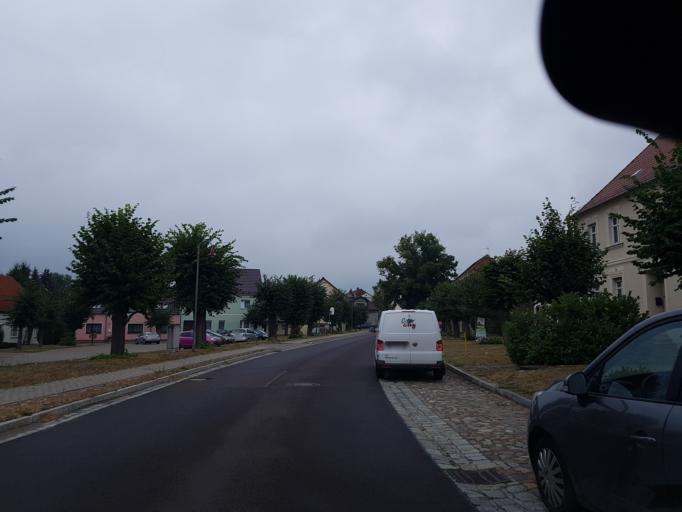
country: DE
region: Brandenburg
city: Gorzke
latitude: 52.1723
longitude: 12.3706
